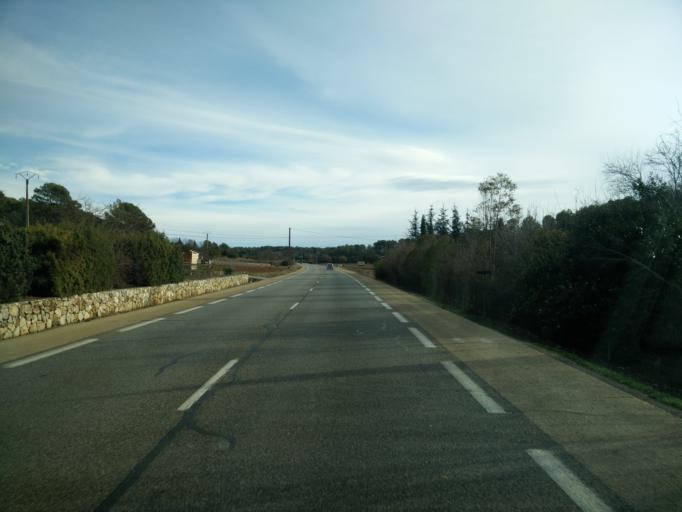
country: FR
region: Provence-Alpes-Cote d'Azur
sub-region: Departement du Var
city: Lorgues
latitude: 43.4710
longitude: 6.3810
